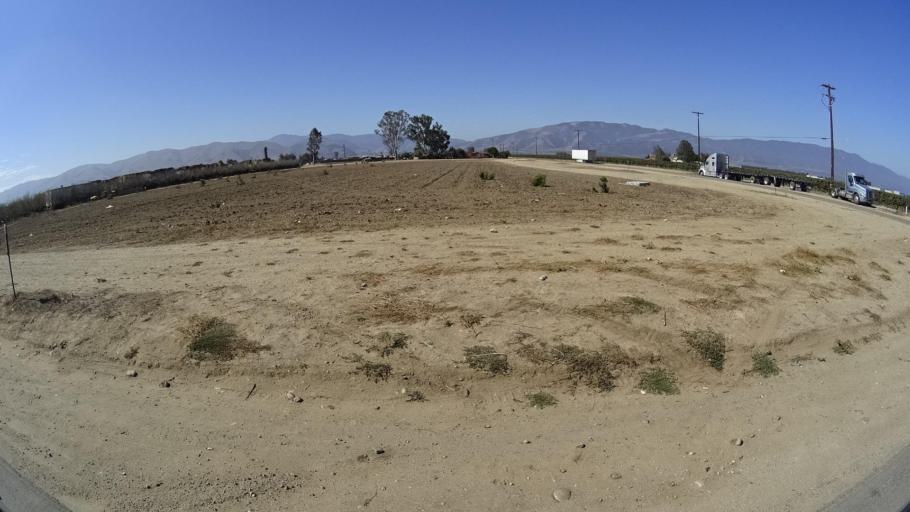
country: US
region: California
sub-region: Monterey County
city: Greenfield
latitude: 36.3224
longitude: -121.2555
